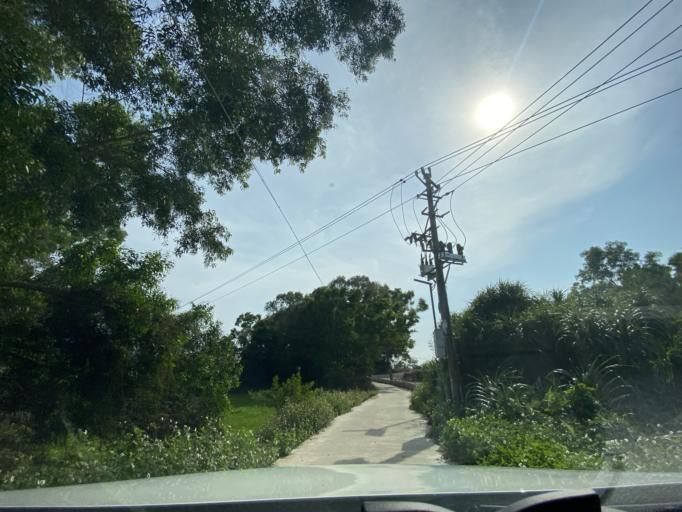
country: CN
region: Hainan
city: Yingzhou
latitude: 18.4101
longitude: 109.8325
